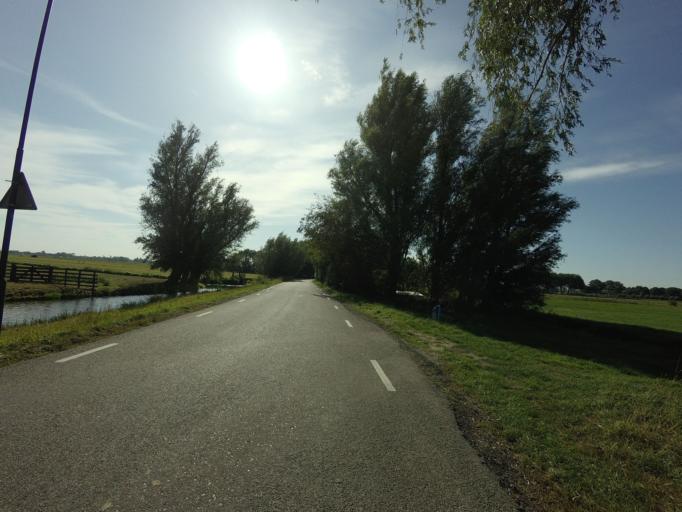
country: NL
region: South Holland
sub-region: Gemeente Gorinchem
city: Gorinchem
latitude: 51.8741
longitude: 5.0227
